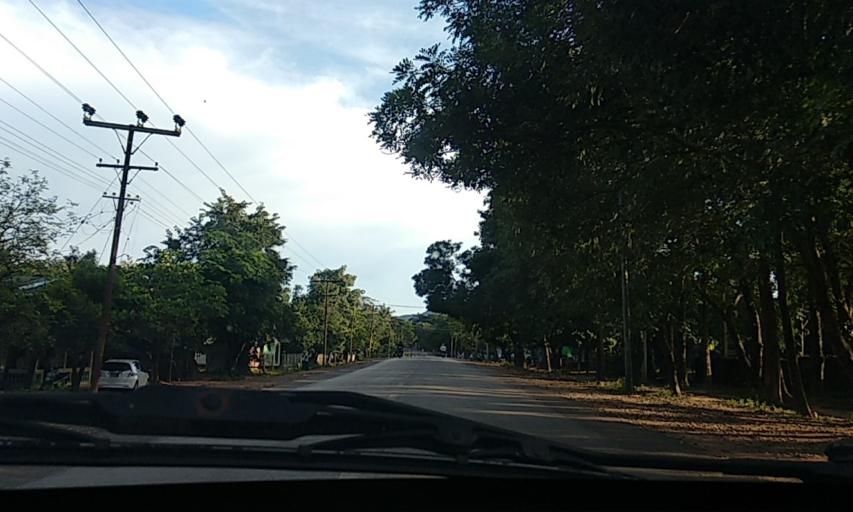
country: MM
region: Mon
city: Mawlamyine
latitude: 16.4052
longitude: 97.7018
